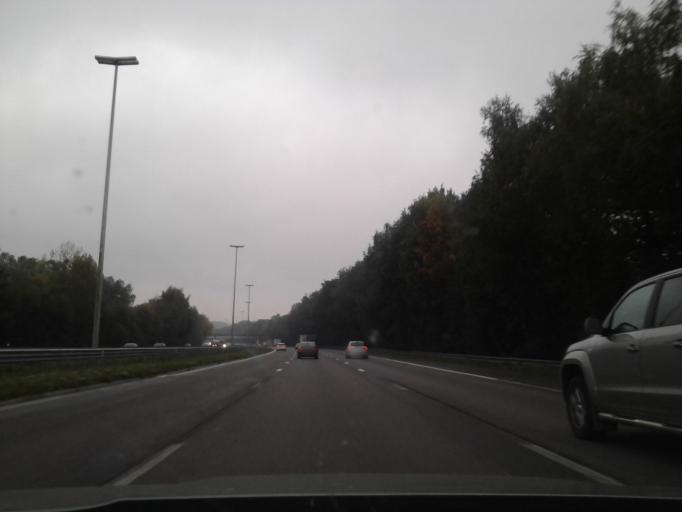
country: BE
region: Wallonia
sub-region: Province du Brabant Wallon
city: Nivelles
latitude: 50.6093
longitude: 4.2964
